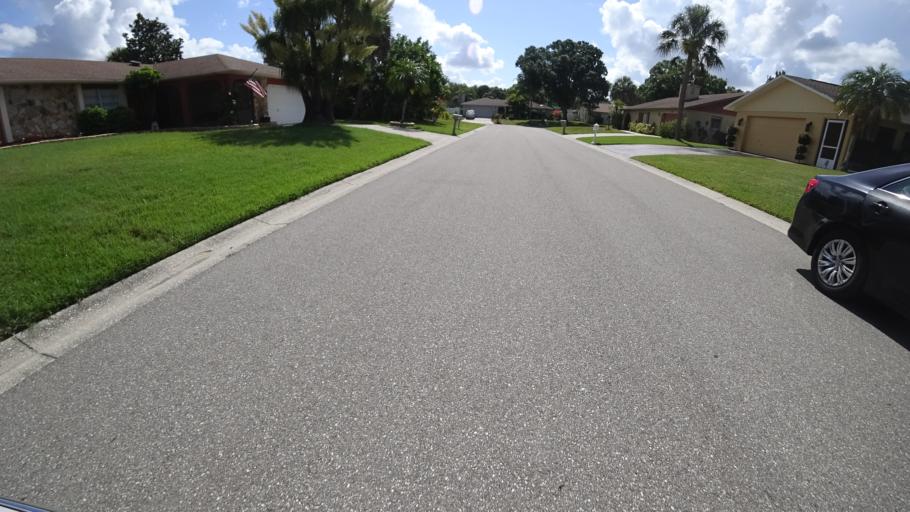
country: US
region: Florida
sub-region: Sarasota County
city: Desoto Lakes
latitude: 27.3899
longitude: -82.4974
